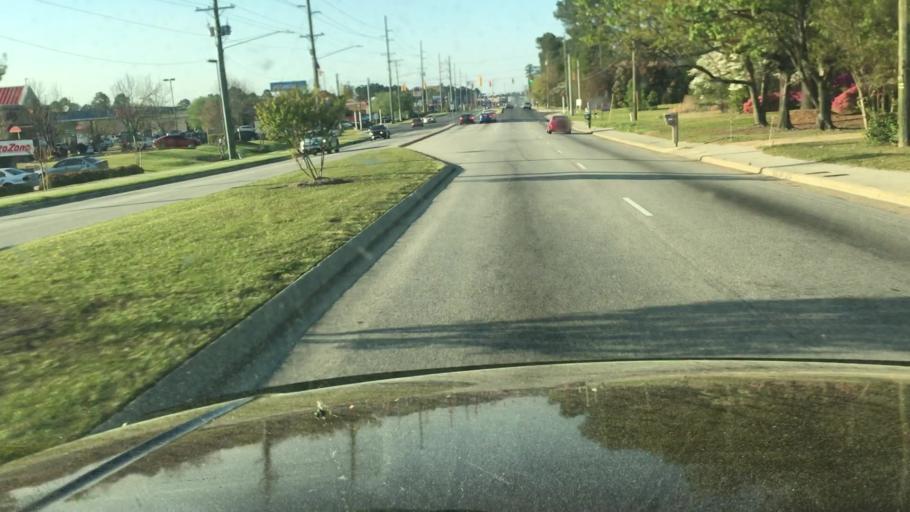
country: US
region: North Carolina
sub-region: Cumberland County
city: Fayetteville
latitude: 35.1223
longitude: -78.8795
